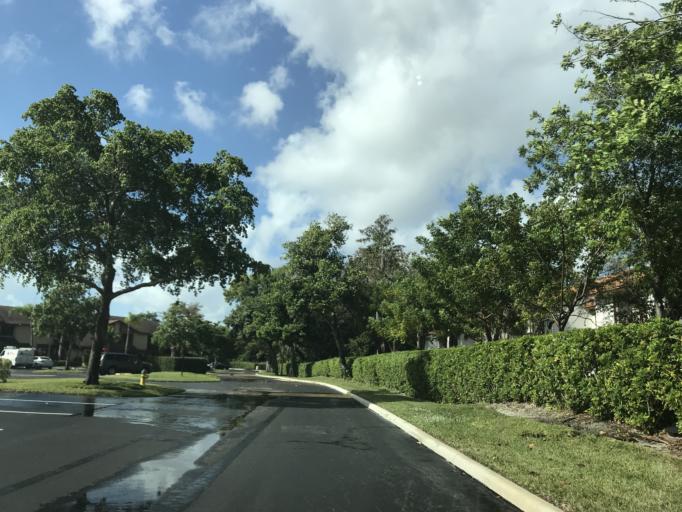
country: US
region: Florida
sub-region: Broward County
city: Coconut Creek
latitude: 26.2709
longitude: -80.1897
